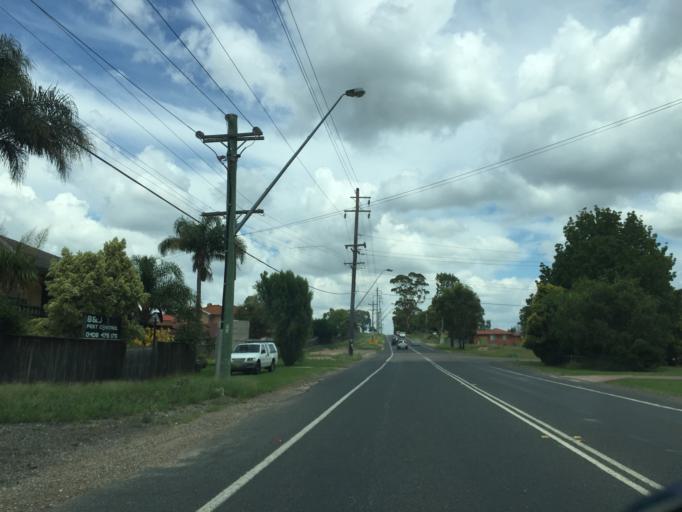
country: AU
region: New South Wales
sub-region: The Hills Shire
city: Beaumont Hills
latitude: -33.6978
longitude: 150.9648
